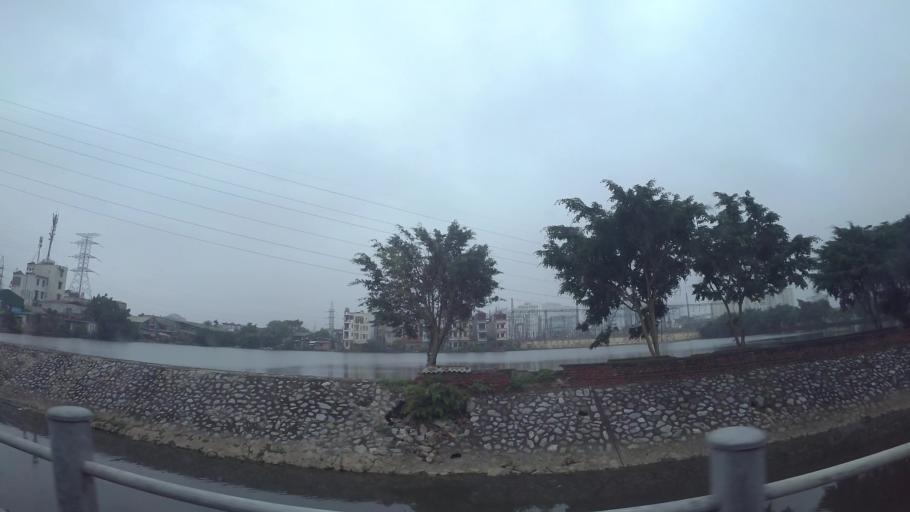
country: VN
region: Ha Noi
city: Hai BaTrung
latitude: 20.9793
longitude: 105.8662
